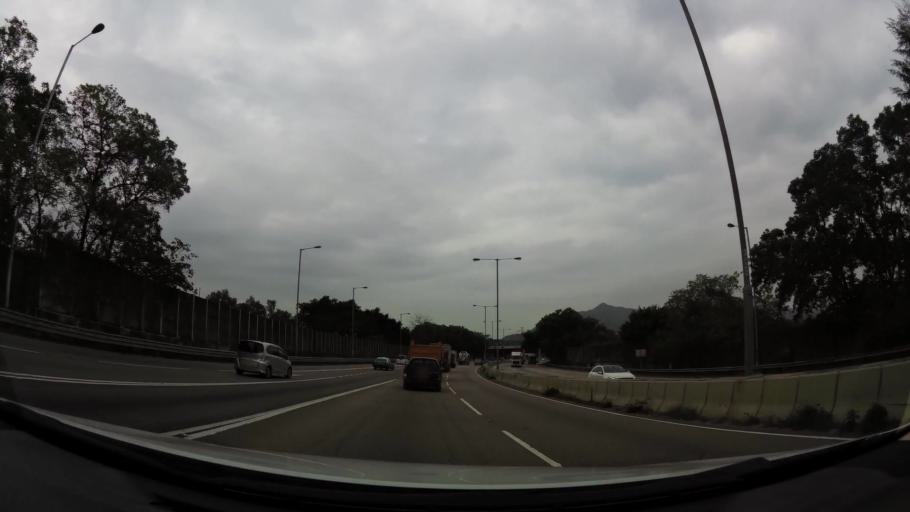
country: HK
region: Yuen Long
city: Yuen Long Kau Hui
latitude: 22.4470
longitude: 114.0402
